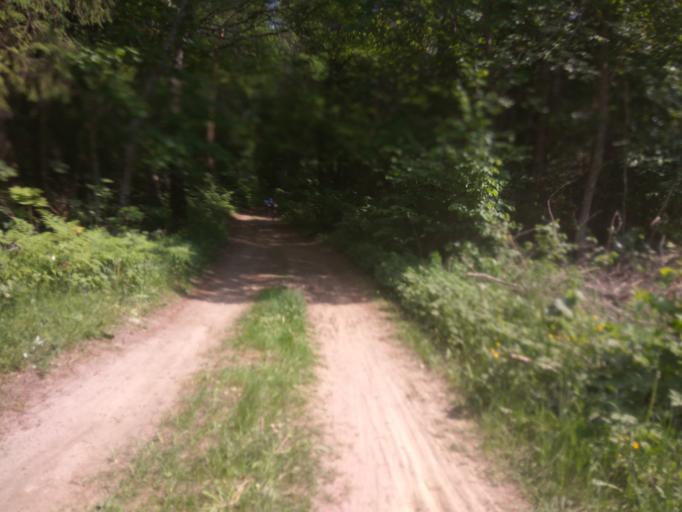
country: LV
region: Kuldigas Rajons
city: Kuldiga
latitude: 56.9038
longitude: 21.9399
